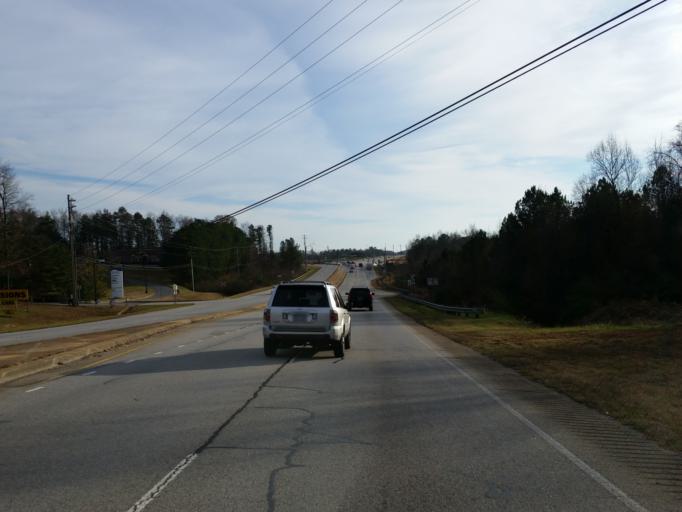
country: US
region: Georgia
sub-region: Paulding County
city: Hiram
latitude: 33.9063
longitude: -84.7790
